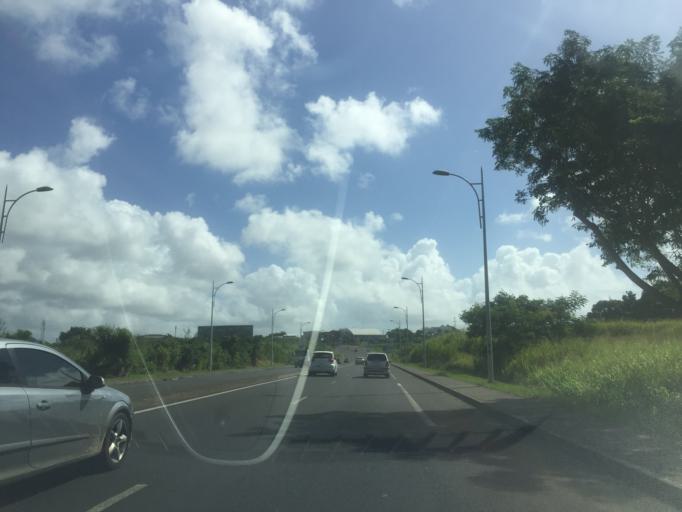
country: GP
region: Guadeloupe
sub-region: Guadeloupe
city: Baie-Mahault
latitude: 16.2398
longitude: -61.5780
